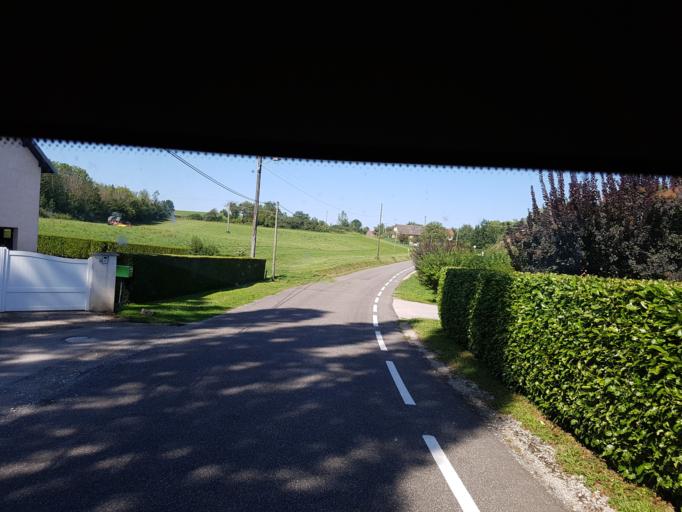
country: FR
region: Franche-Comte
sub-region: Departement du Jura
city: Perrigny
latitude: 46.7301
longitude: 5.5793
